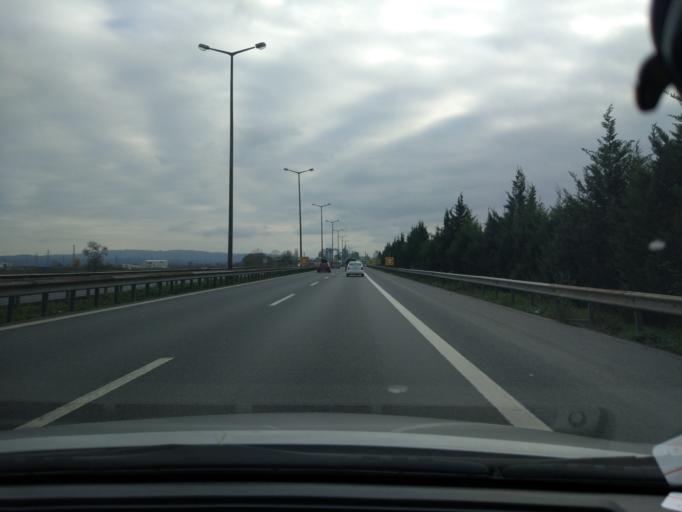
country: TR
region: Kocaeli
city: Kosekoy
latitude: 40.7672
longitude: 30.0180
